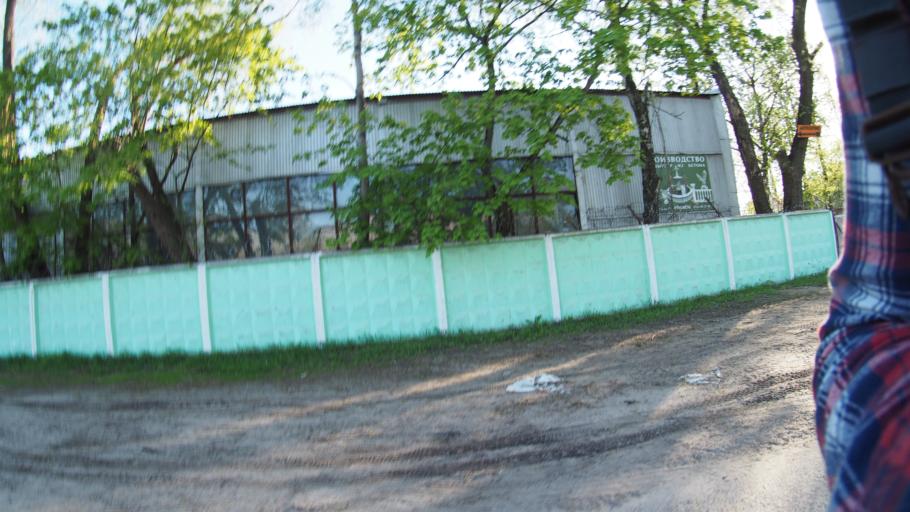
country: RU
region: Moskovskaya
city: Ramenskoye
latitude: 55.5579
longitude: 38.2127
